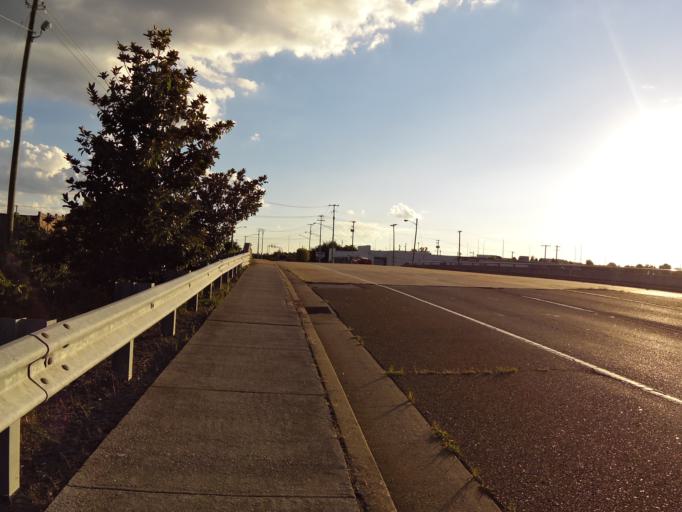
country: US
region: Tennessee
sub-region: Knox County
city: Knoxville
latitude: 35.9766
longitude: -83.9137
